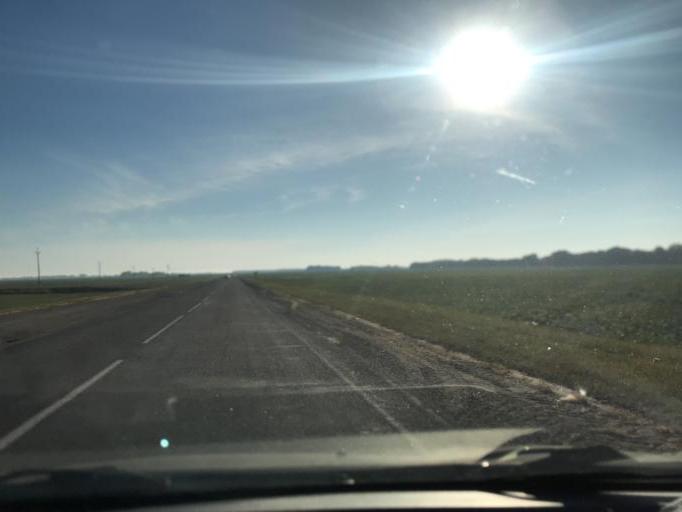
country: BY
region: Gomel
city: Brahin
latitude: 51.7975
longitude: 30.1429
